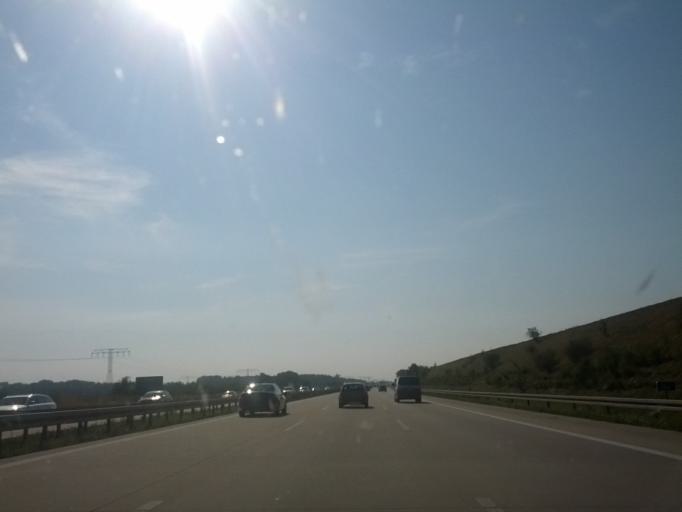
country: DE
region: Brandenburg
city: Neuenhagen
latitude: 52.5319
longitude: 13.7066
